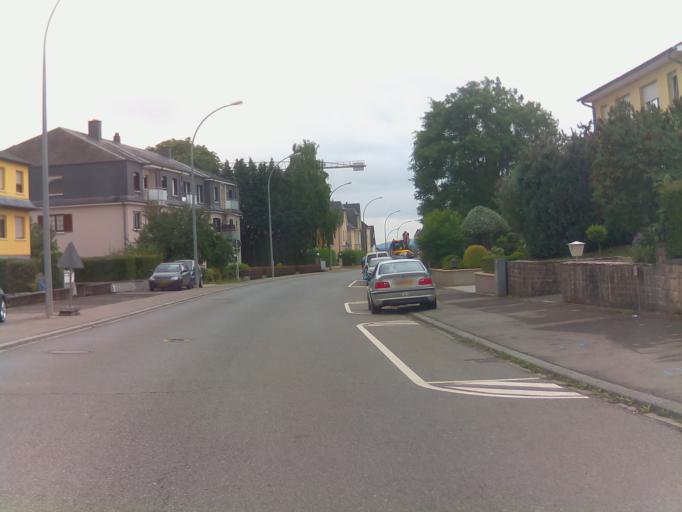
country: LU
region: Luxembourg
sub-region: Canton de Capellen
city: Dippach
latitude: 49.5752
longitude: 5.9945
